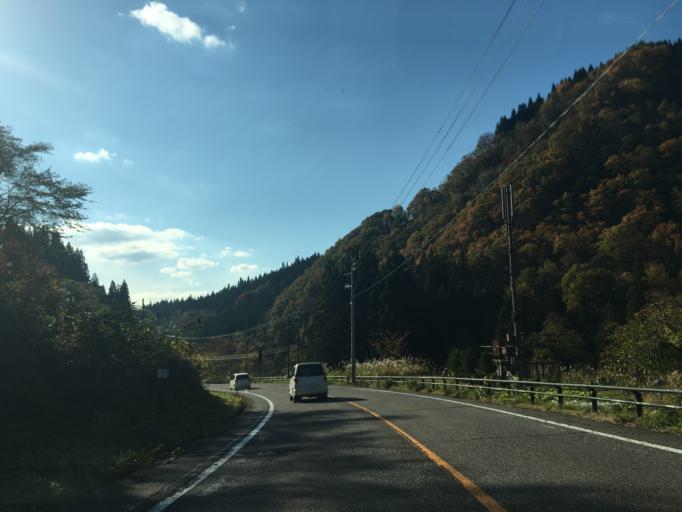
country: JP
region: Fukushima
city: Kitakata
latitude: 37.5762
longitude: 139.6888
